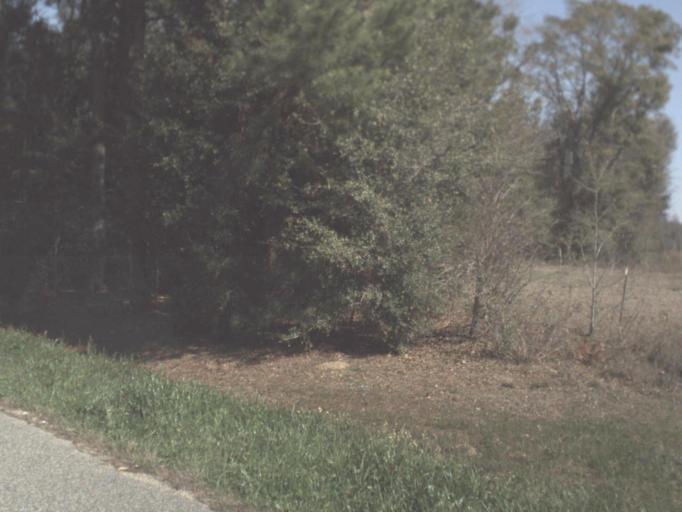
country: US
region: Florida
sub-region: Calhoun County
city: Blountstown
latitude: 30.5834
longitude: -85.0219
